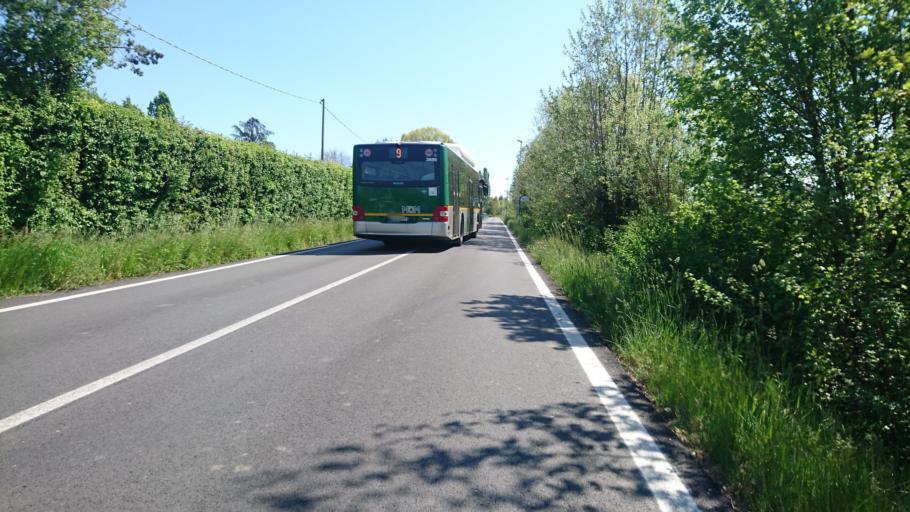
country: IT
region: Veneto
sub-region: Provincia di Treviso
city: Dosson
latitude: 45.6286
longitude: 12.2693
